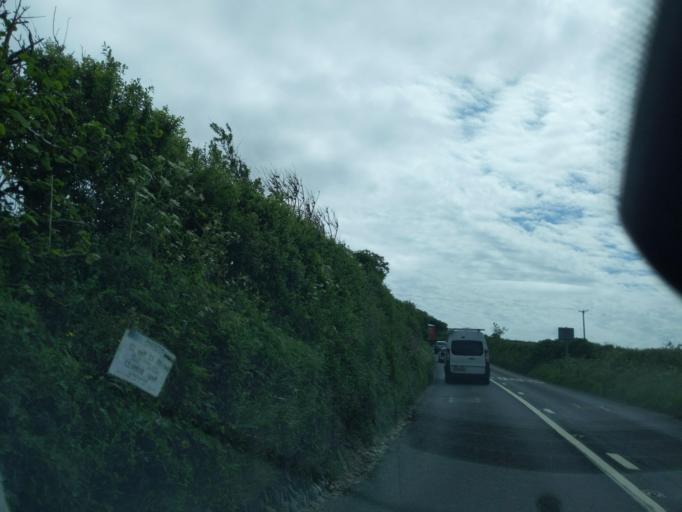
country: GB
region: England
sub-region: Cornwall
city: Perranporth
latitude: 50.3221
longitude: -5.1355
